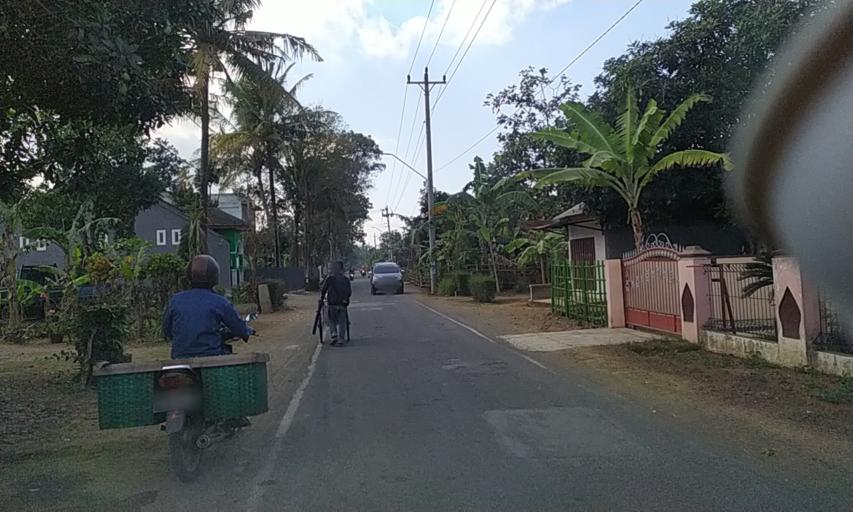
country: ID
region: Central Java
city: Adipala
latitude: -7.6627
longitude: 109.1578
